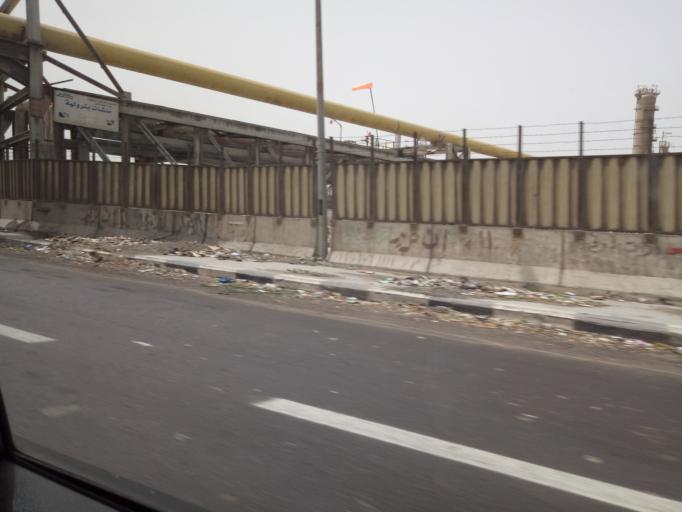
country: EG
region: Alexandria
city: Alexandria
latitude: 31.1350
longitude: 29.8518
